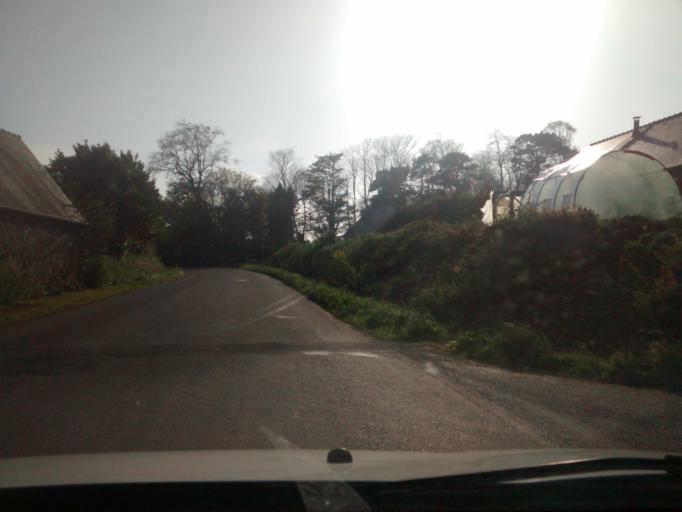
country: FR
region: Brittany
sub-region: Departement des Cotes-d'Armor
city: Penvenan
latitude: 48.8191
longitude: -3.2873
